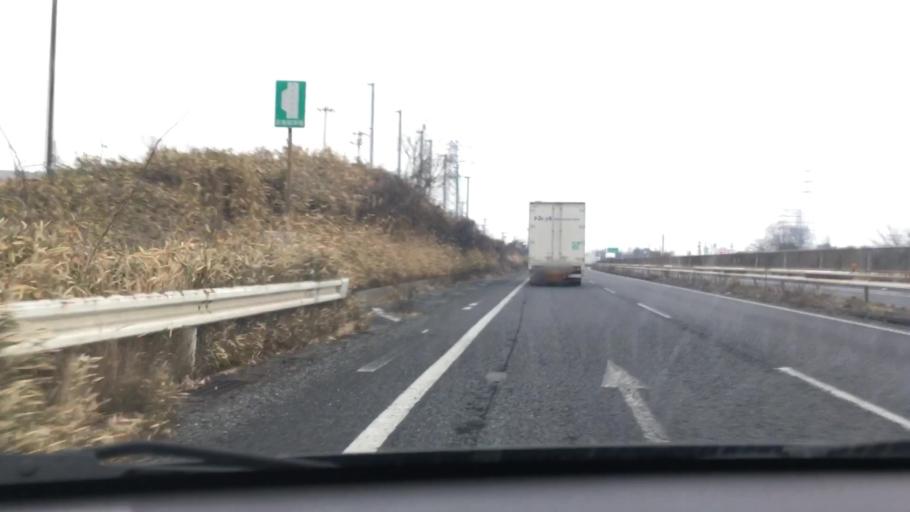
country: JP
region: Mie
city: Ueno-ebisumachi
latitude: 34.7184
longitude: 136.0815
